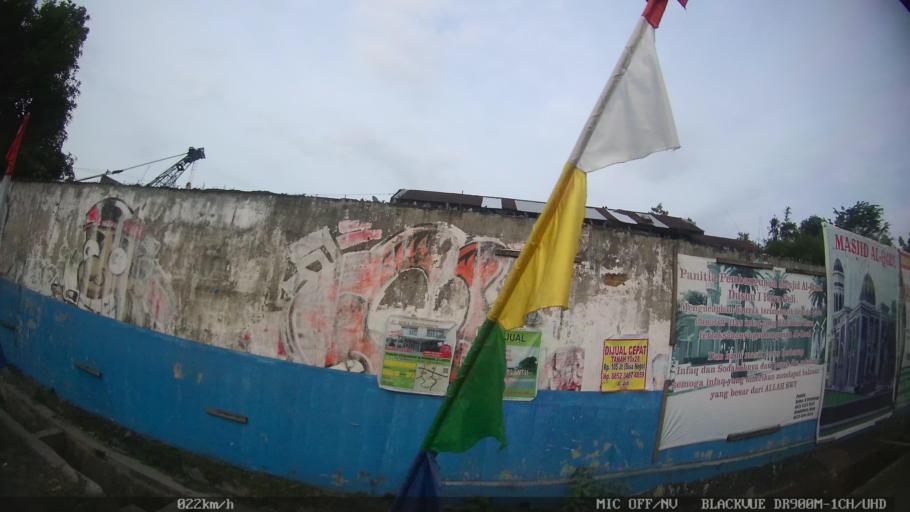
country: ID
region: North Sumatra
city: Sunggal
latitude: 3.5969
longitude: 98.6028
